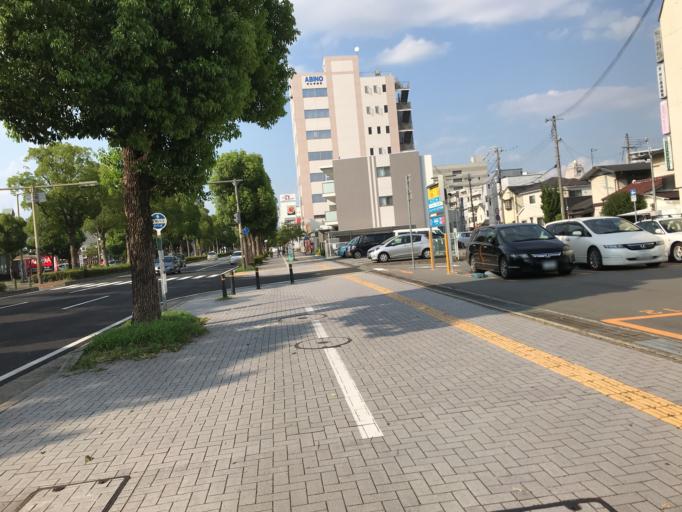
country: JP
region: Hyogo
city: Himeji
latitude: 34.8175
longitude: 134.6854
